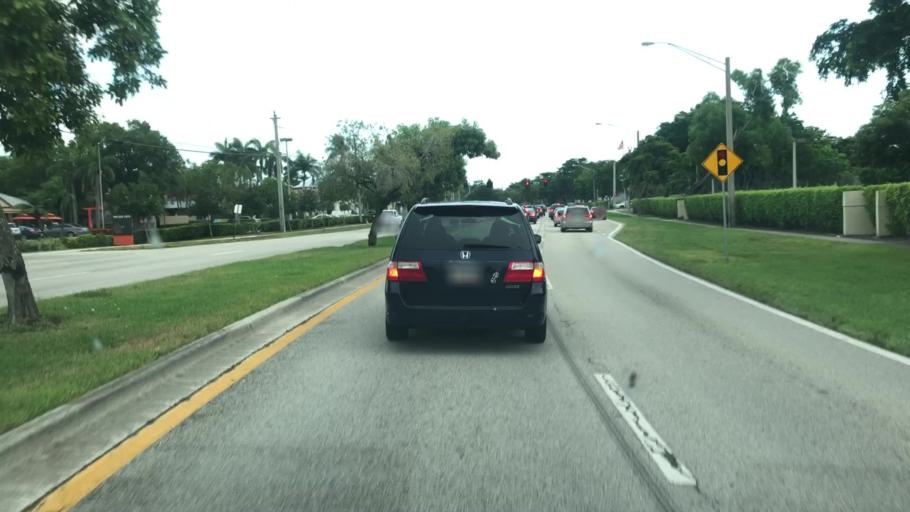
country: US
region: Florida
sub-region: Broward County
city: Tedder
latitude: 26.3005
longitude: -80.1347
